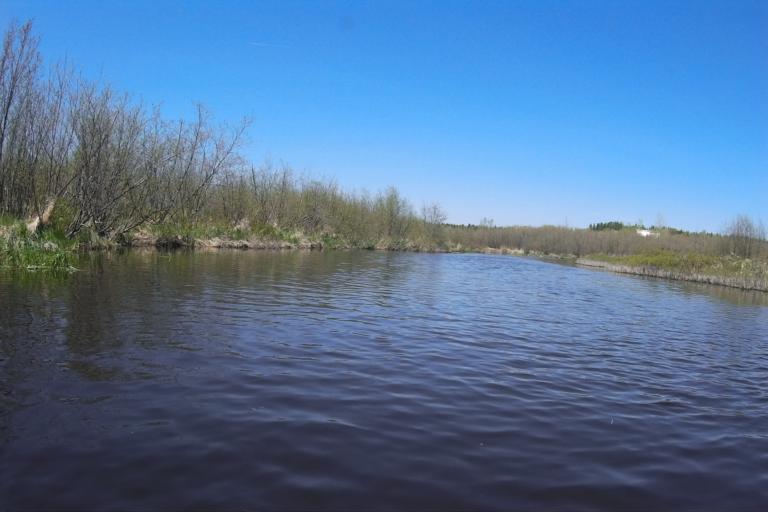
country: CA
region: Ontario
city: Powassan
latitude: 46.1550
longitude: -79.2398
